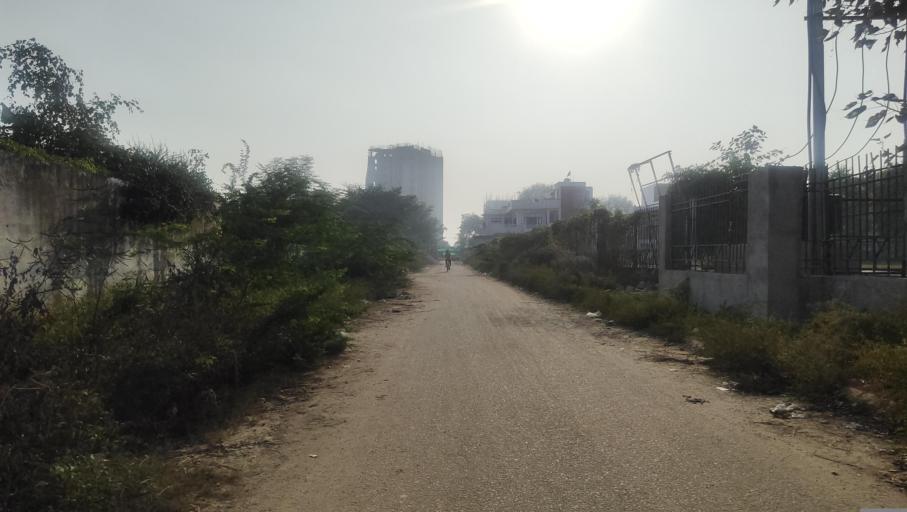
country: IN
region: Uttar Pradesh
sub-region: Lucknow District
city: Goshainganj
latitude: 26.7918
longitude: 81.0123
